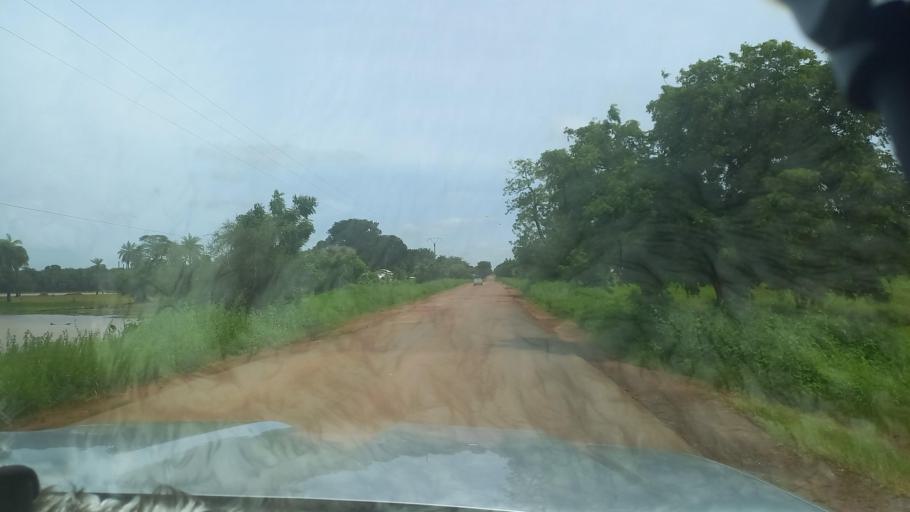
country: SN
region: Kolda
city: Marsassoum
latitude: 12.9662
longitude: -15.9640
